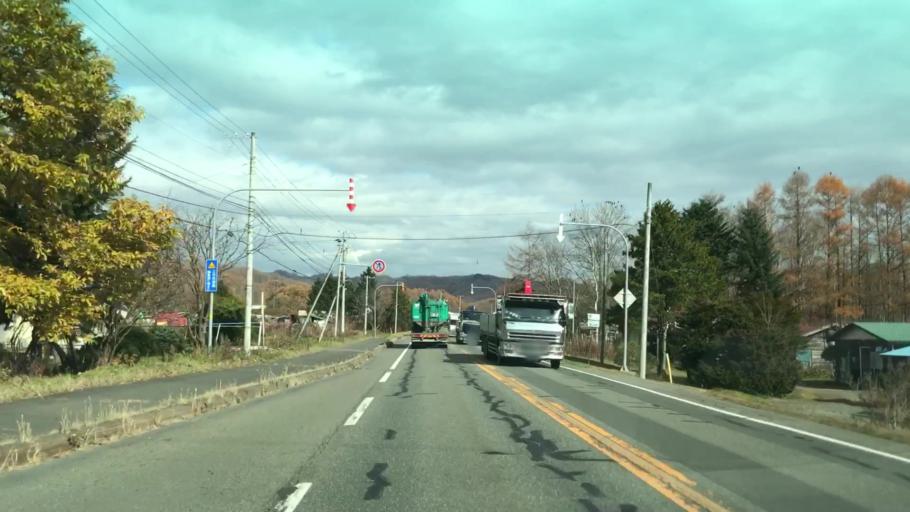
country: JP
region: Hokkaido
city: Shizunai-furukawacho
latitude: 42.6983
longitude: 142.2239
